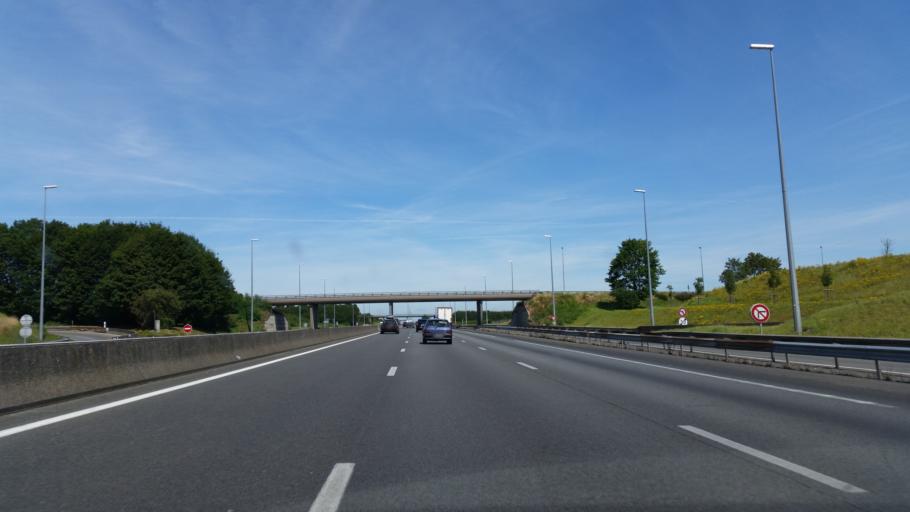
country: FR
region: Nord-Pas-de-Calais
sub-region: Departement du Pas-de-Calais
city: Fampoux
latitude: 50.2684
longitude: 2.8678
